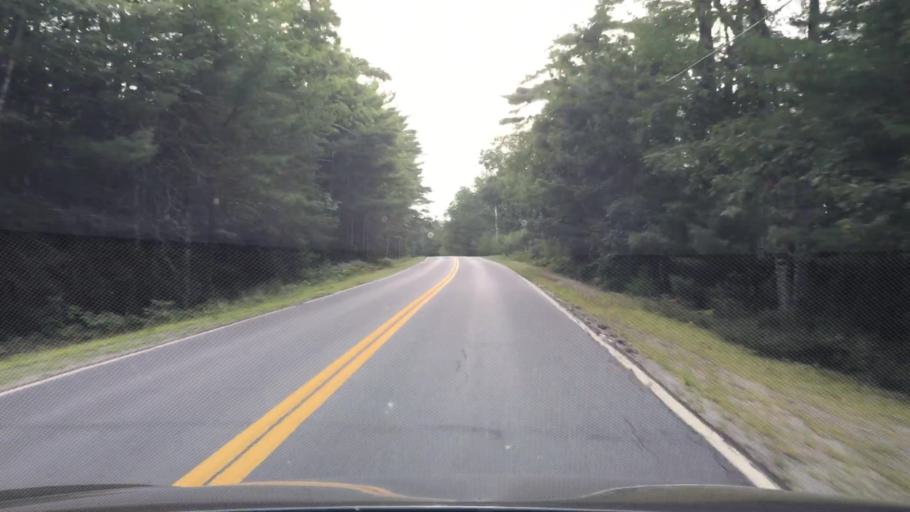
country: US
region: Maine
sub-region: Hancock County
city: Penobscot
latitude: 44.4510
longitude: -68.6891
